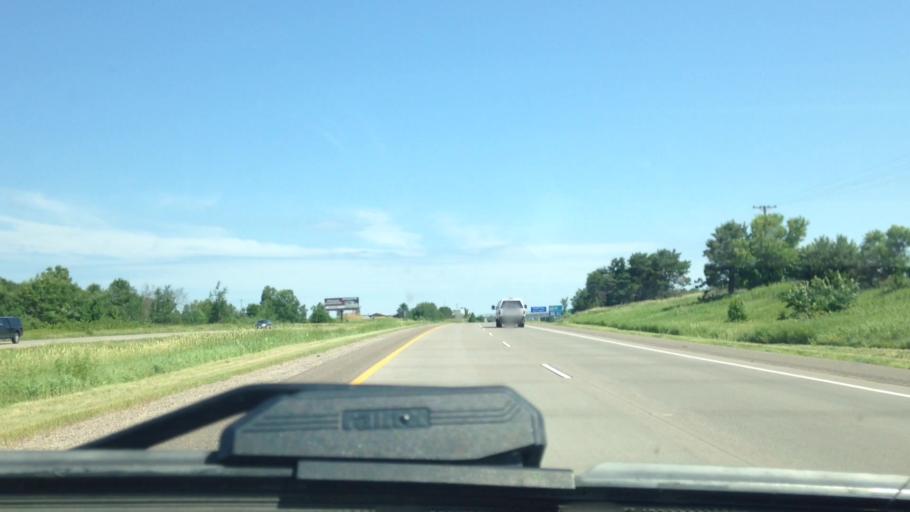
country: US
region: Wisconsin
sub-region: Barron County
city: Rice Lake
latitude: 45.4964
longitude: -91.7641
